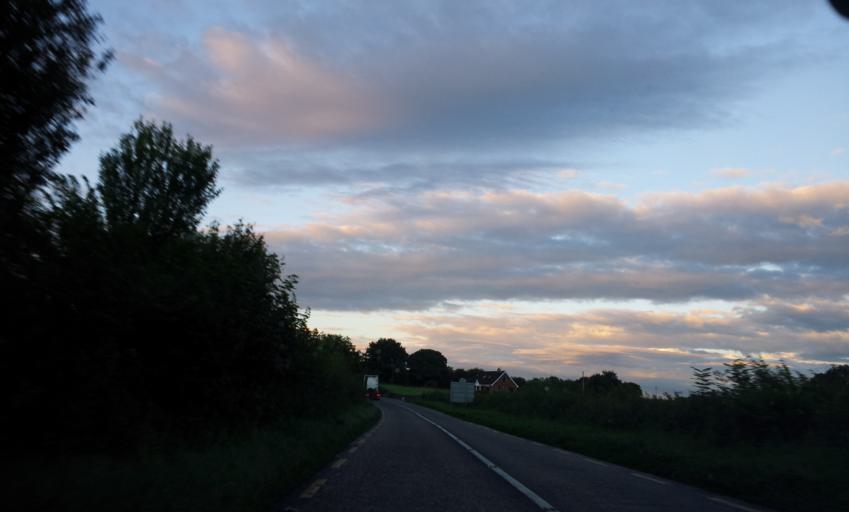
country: IE
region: Munster
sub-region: County Limerick
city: Adare
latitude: 52.5508
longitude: -8.8147
